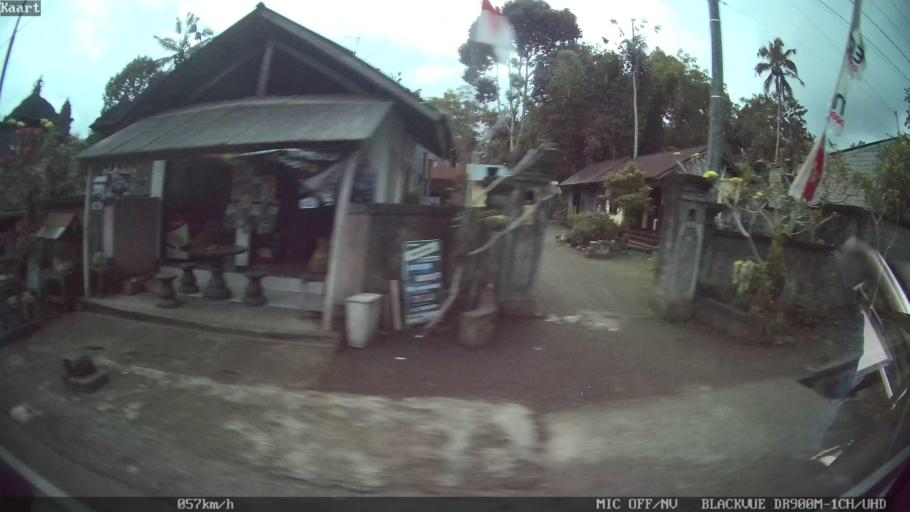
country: ID
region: Bali
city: Banjar Tiga
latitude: -8.3793
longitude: 115.4179
